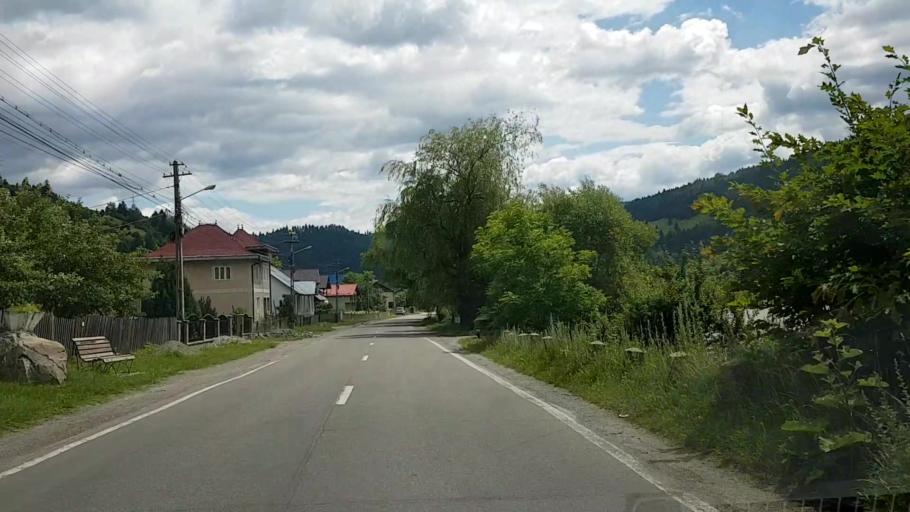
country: RO
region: Suceava
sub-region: Comuna Brosteni
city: Brosteni
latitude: 47.2419
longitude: 25.7067
